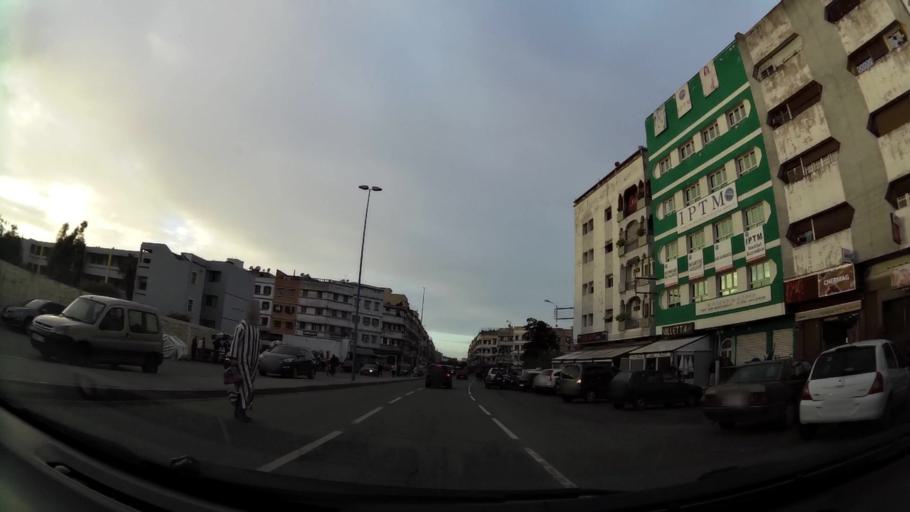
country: MA
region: Grand Casablanca
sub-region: Casablanca
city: Casablanca
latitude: 33.5588
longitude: -7.6008
